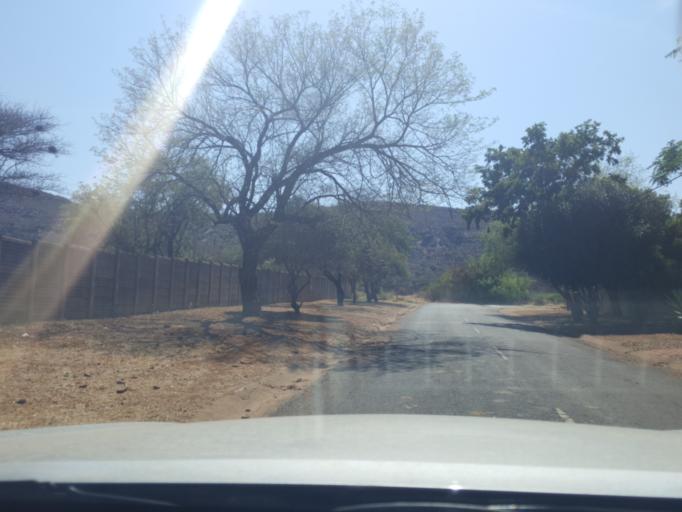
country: ZA
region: North-West
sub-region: Ngaka Modiri Molema District Municipality
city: Zeerust
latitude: -25.5247
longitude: 26.0789
